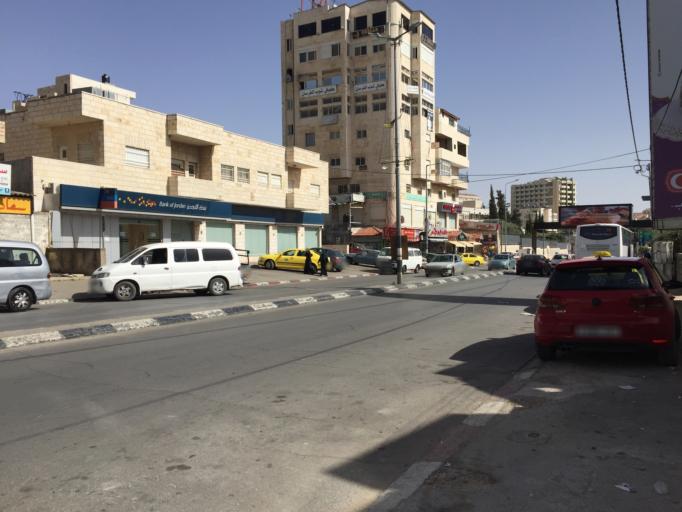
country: PS
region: West Bank
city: Bethlehem
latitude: 31.7124
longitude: 35.1992
